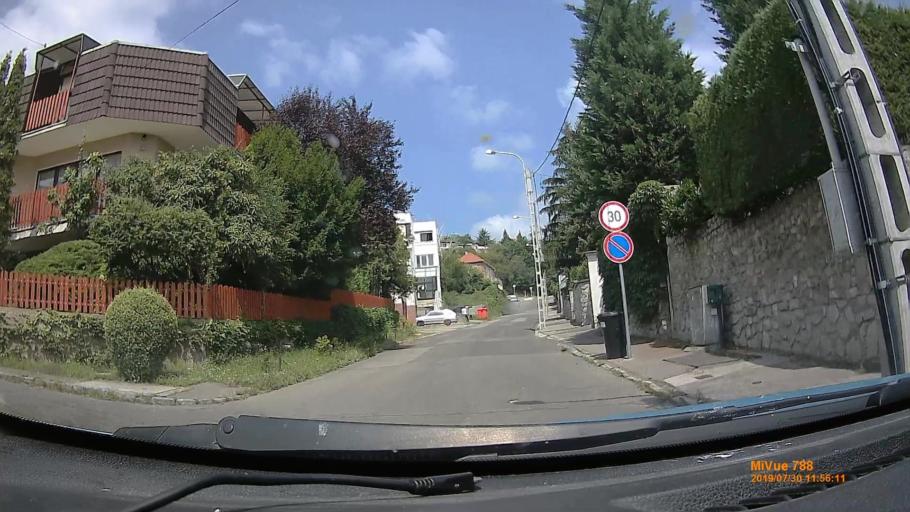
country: HU
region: Baranya
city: Pecs
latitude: 46.0822
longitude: 18.2191
